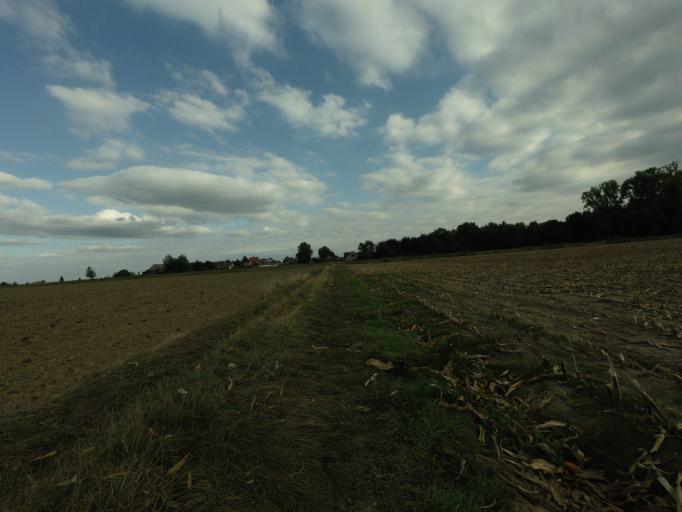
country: BE
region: Flanders
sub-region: Provincie Vlaams-Brabant
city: Steenokkerzeel
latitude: 50.9329
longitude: 4.5206
